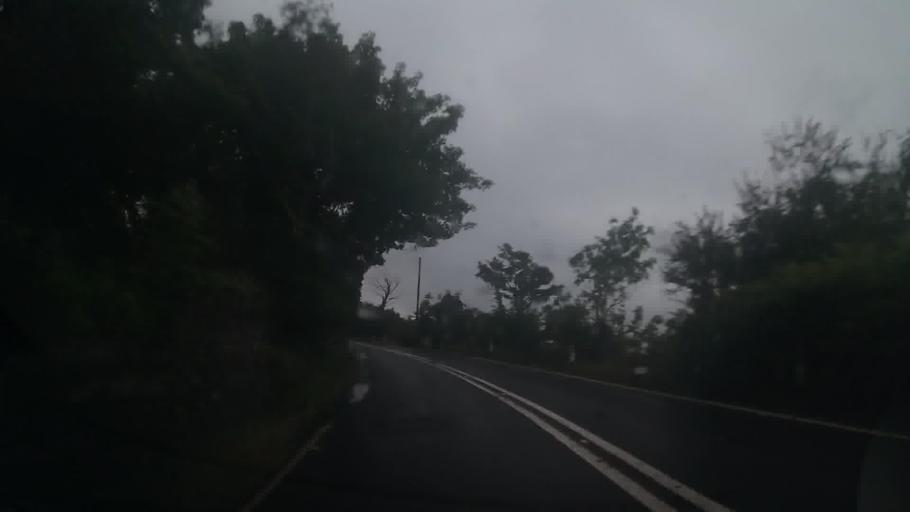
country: GB
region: Scotland
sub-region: North Ayrshire
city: Skelmorlie
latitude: 55.8454
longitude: -4.8889
